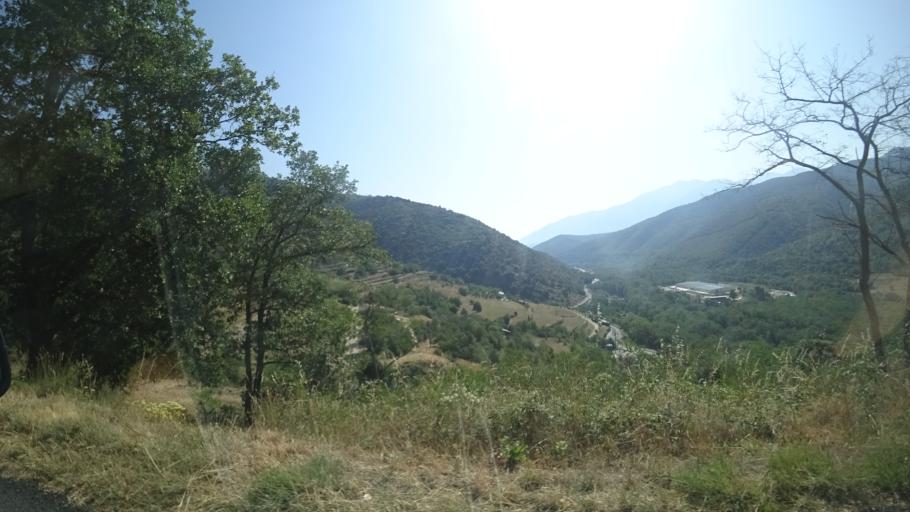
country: FR
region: Languedoc-Roussillon
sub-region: Departement des Pyrenees-Orientales
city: Vernet-les-Bains
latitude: 42.5620
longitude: 2.2854
